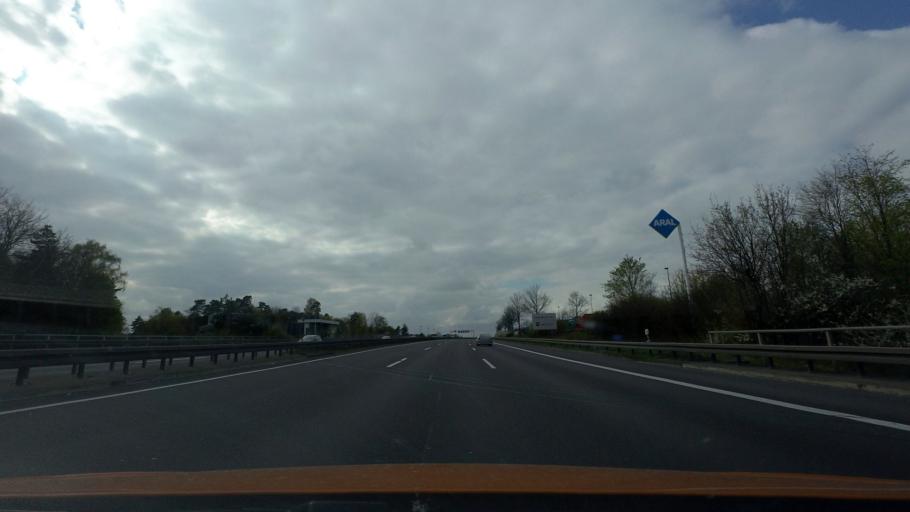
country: DE
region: Saxony-Anhalt
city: Harbke
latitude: 52.2190
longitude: 11.0593
